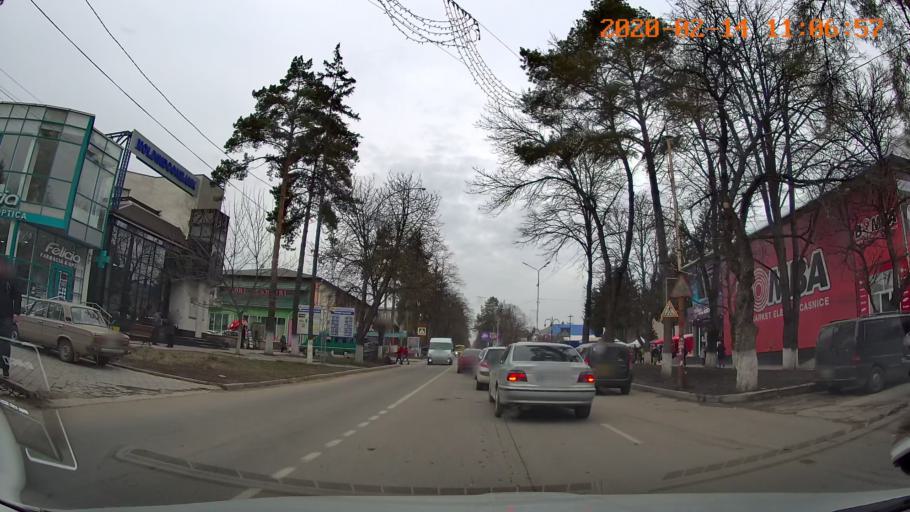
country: MD
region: Raionul Edinet
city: Edinet
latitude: 48.1689
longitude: 27.3069
